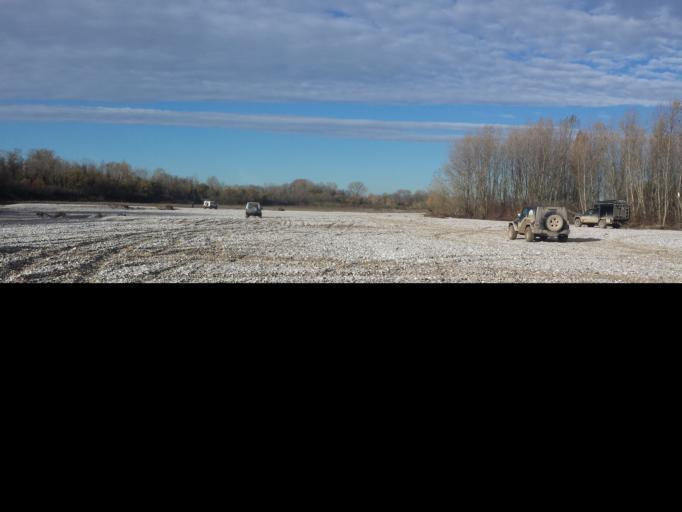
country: IT
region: Friuli Venezia Giulia
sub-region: Provincia di Udine
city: San Vito al Torre
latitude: 45.9006
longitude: 13.4005
